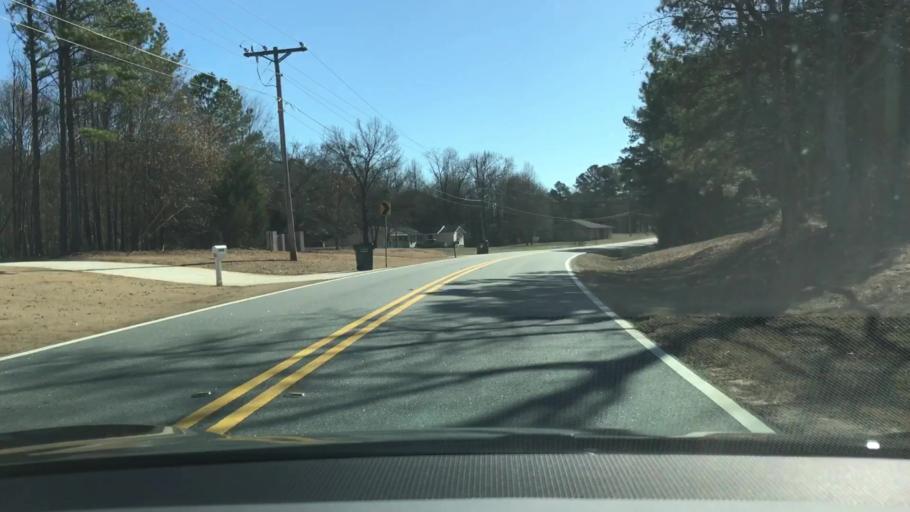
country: US
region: Georgia
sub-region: Walton County
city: Monroe
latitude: 33.8573
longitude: -83.7376
